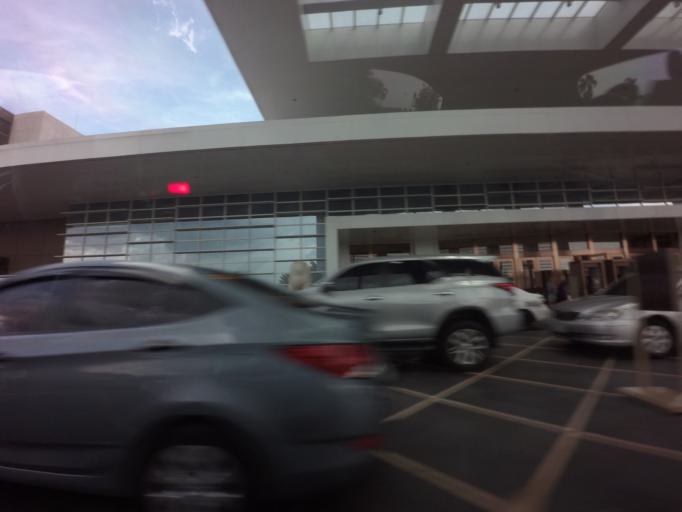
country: PH
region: Metro Manila
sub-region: Makati City
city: Makati City
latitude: 14.5237
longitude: 120.9813
